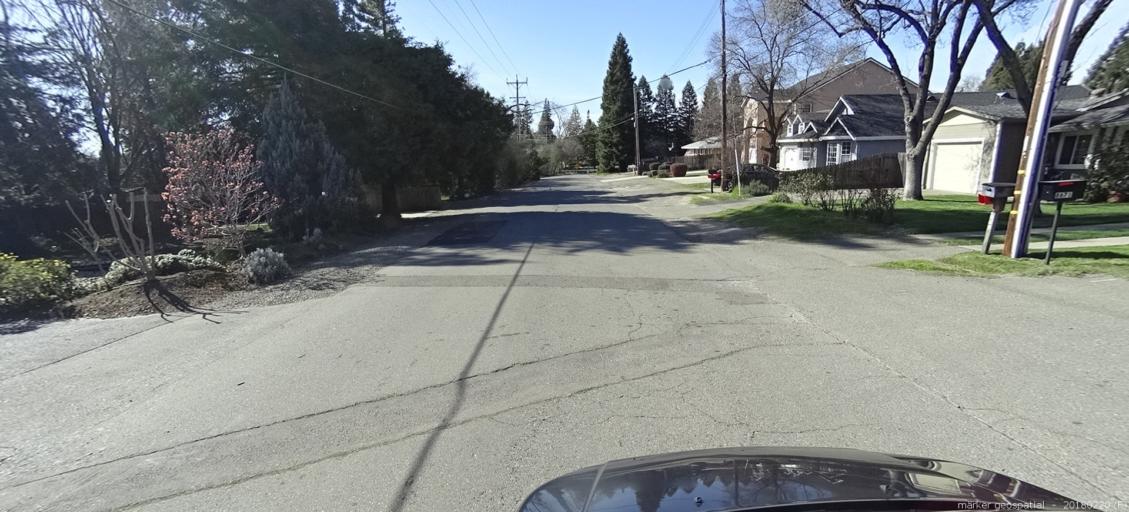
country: US
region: California
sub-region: Sacramento County
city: Orangevale
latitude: 38.6931
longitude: -121.2362
